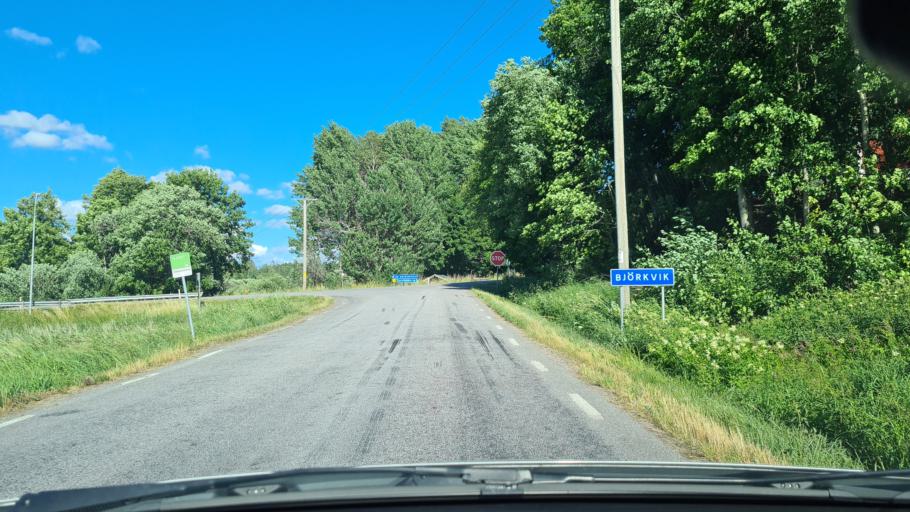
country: SE
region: Soedermanland
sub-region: Nykopings Kommun
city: Olstorp
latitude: 58.8288
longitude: 16.5197
